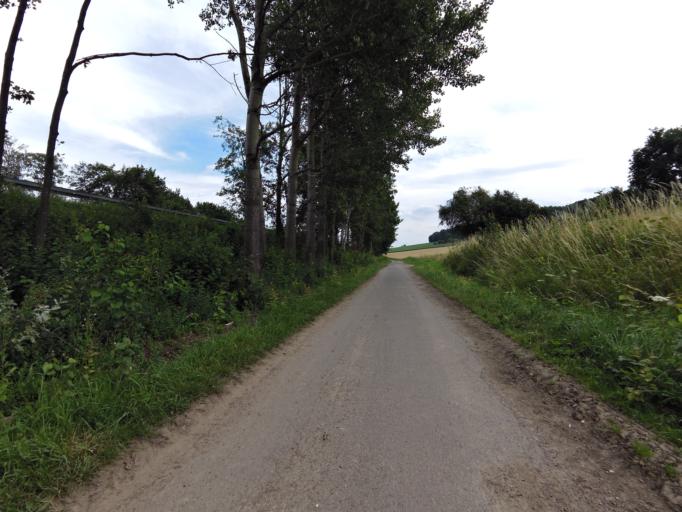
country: NL
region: Limburg
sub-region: Gemeente Vaals
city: Vaals
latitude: 50.8121
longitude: 6.0318
